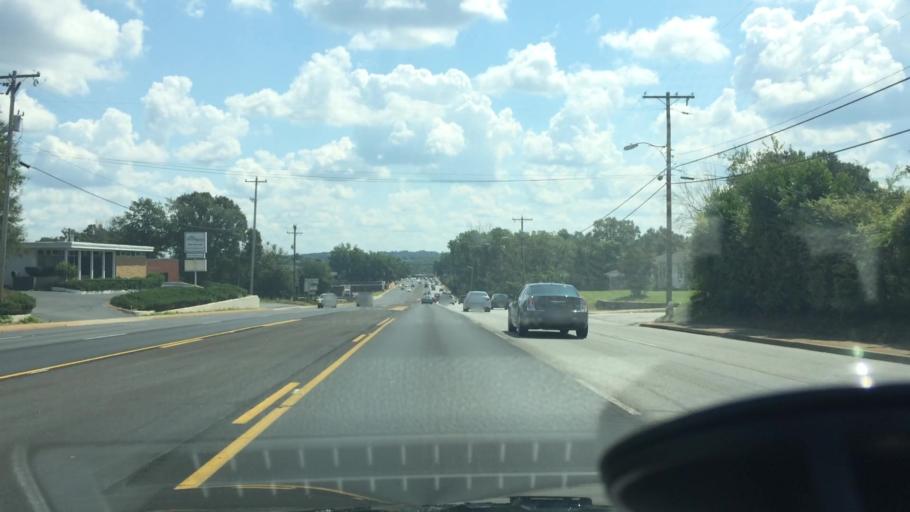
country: US
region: South Carolina
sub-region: Greenville County
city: Wade Hampton
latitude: 34.8840
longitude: -82.3680
